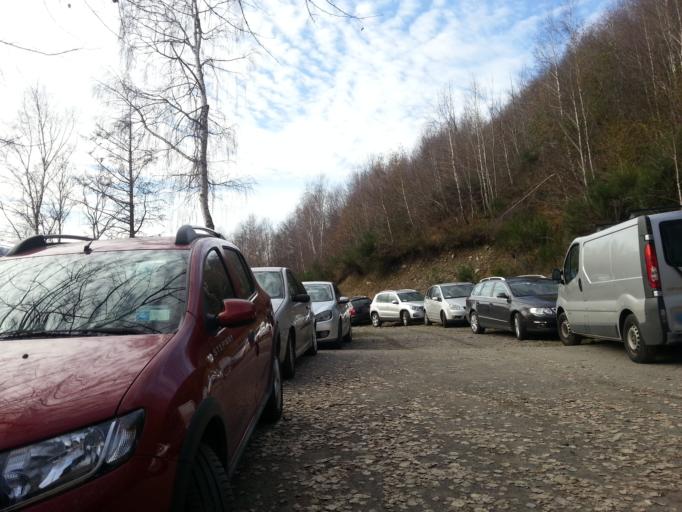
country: IT
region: Lombardy
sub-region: Provincia di Como
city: Plesio
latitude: 46.0600
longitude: 9.2301
